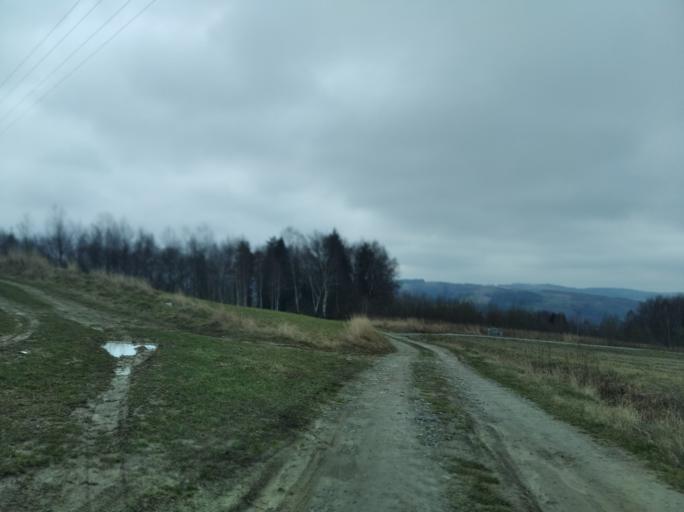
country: PL
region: Subcarpathian Voivodeship
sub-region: Powiat strzyzowski
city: Strzyzow
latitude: 49.9043
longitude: 21.8089
